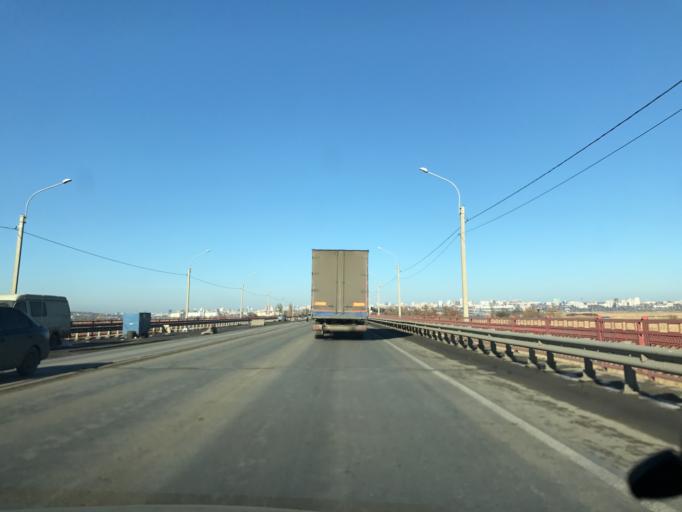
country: RU
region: Rostov
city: Bataysk
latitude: 47.1762
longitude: 39.7421
